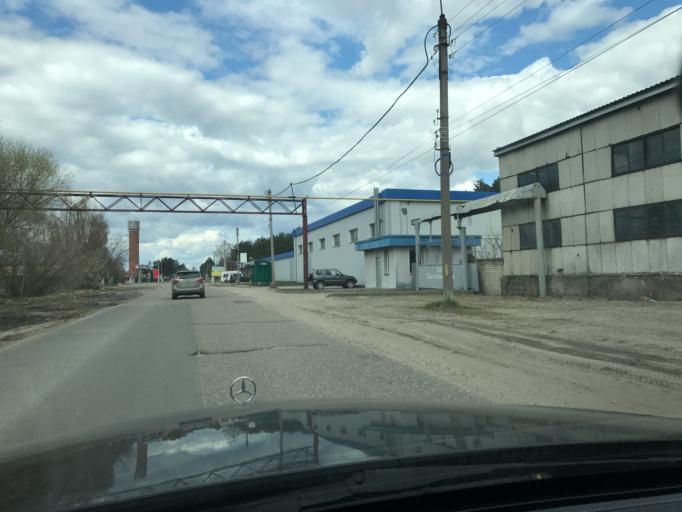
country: RU
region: Vladimir
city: Pokrov
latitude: 55.9003
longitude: 39.1985
